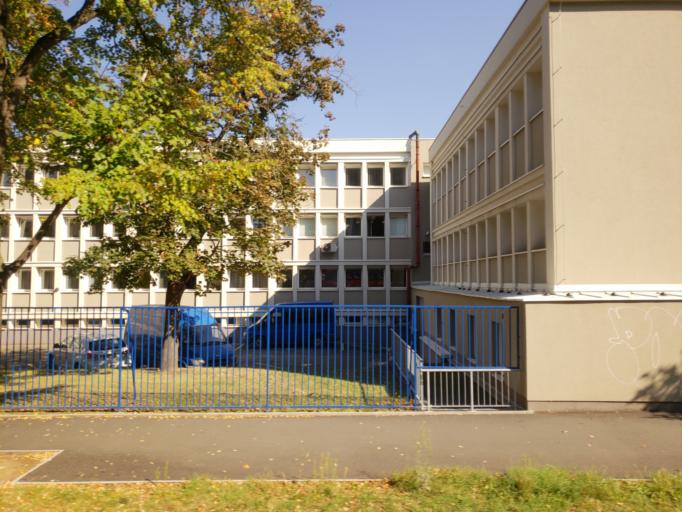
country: CZ
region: Praha
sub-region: Praha 1
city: Mala Strana
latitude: 50.0798
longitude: 14.3900
